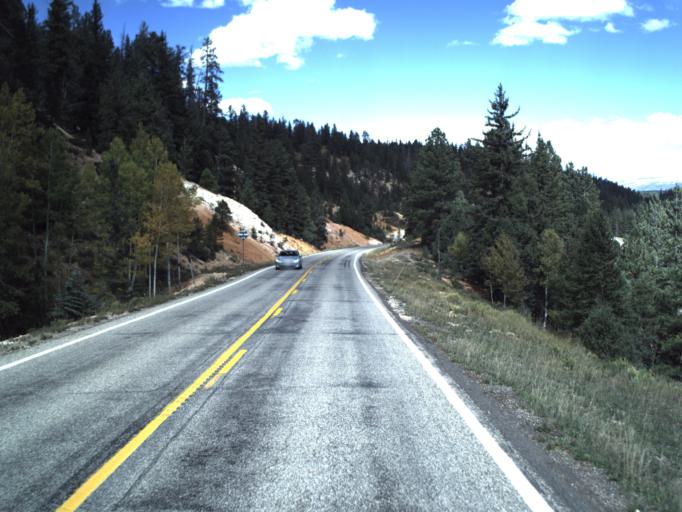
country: US
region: Utah
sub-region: Garfield County
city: Panguitch
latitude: 37.4948
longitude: -112.6063
